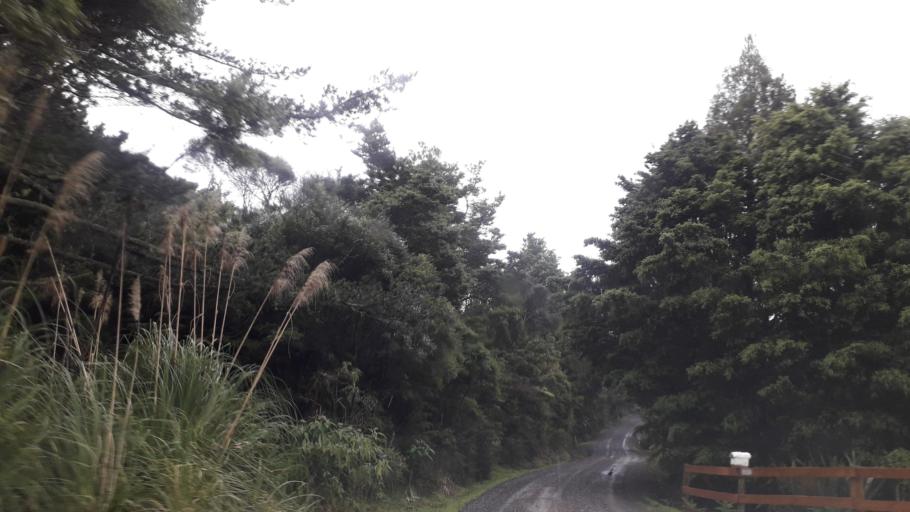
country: NZ
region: Northland
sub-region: Far North District
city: Kaitaia
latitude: -35.3909
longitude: 173.4037
